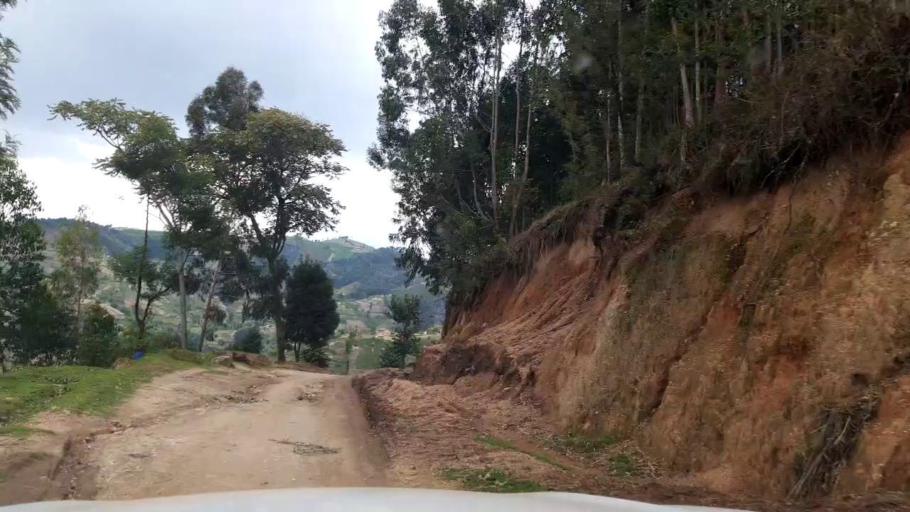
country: RW
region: Western Province
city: Kibuye
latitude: -1.8637
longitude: 29.5541
